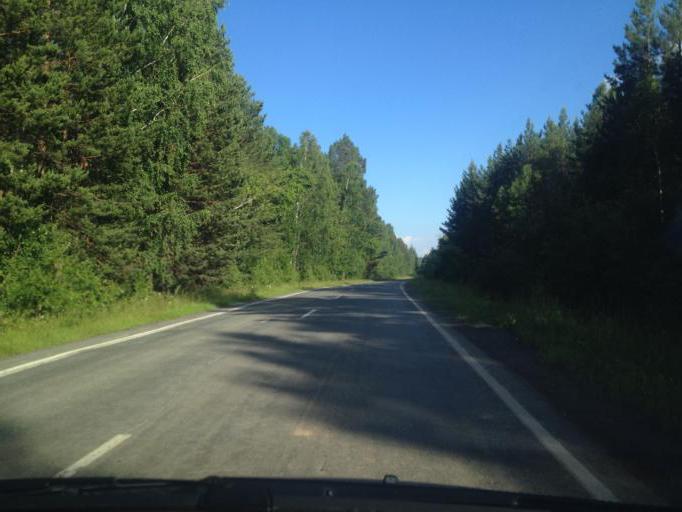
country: RU
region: Chelyabinsk
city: Cheremshanka
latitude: 56.2528
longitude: 60.3512
